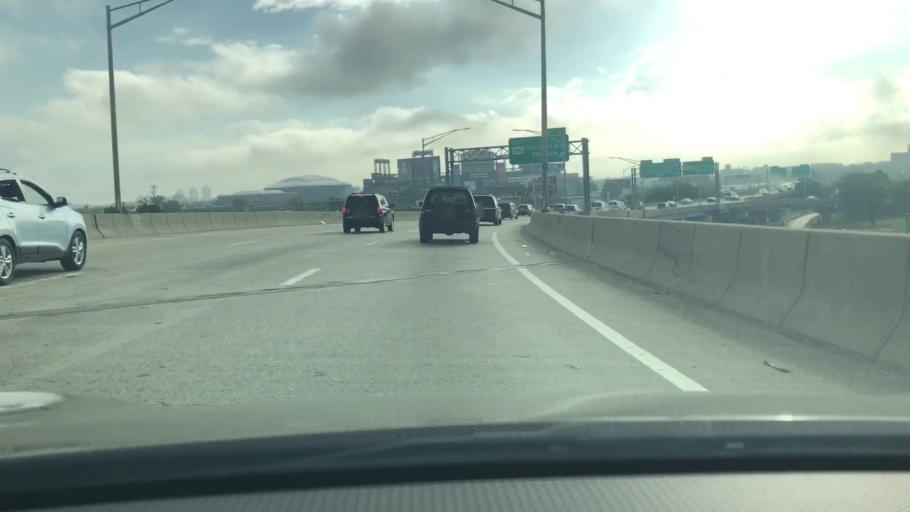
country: US
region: New York
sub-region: Queens County
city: Jamaica
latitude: 40.7645
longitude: -73.8407
